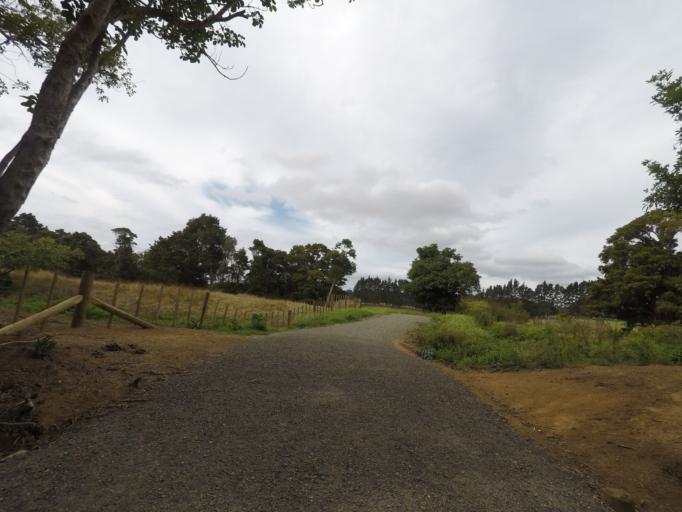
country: NZ
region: Northland
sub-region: Whangarei
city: Whangarei
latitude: -35.6760
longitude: 174.3324
